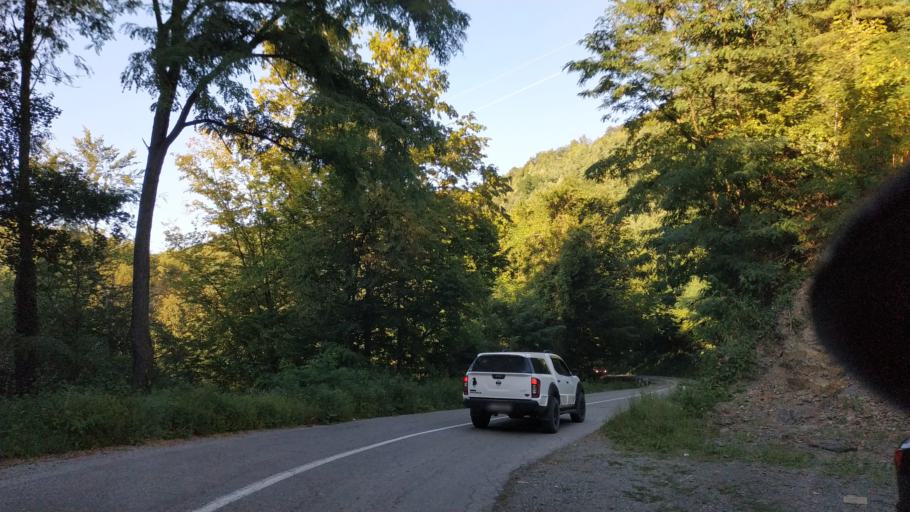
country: RS
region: Central Serbia
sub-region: Rasinski Okrug
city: Krusevac
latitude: 43.4585
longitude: 21.3589
